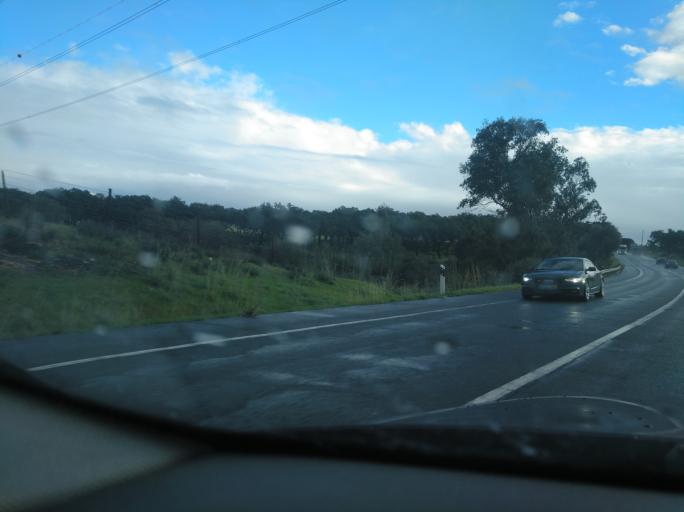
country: PT
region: Setubal
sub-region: Grandola
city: Grandola
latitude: 38.0207
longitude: -8.3990
